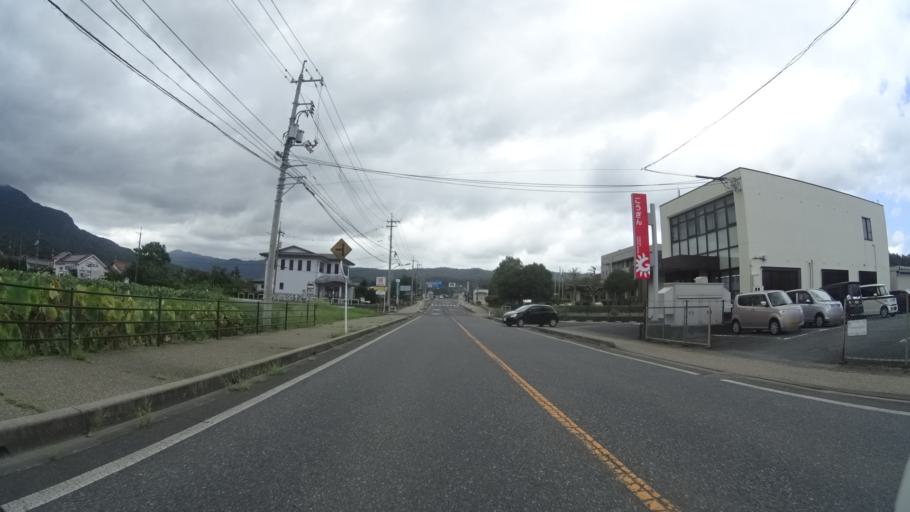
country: JP
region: Tottori
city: Tottori
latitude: 35.4640
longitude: 134.0615
